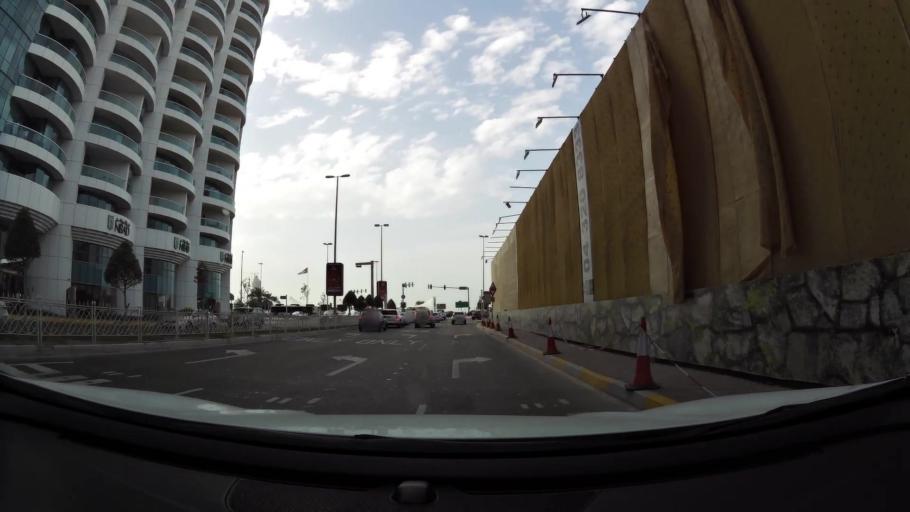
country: AE
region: Abu Dhabi
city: Abu Dhabi
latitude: 24.4724
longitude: 54.3416
